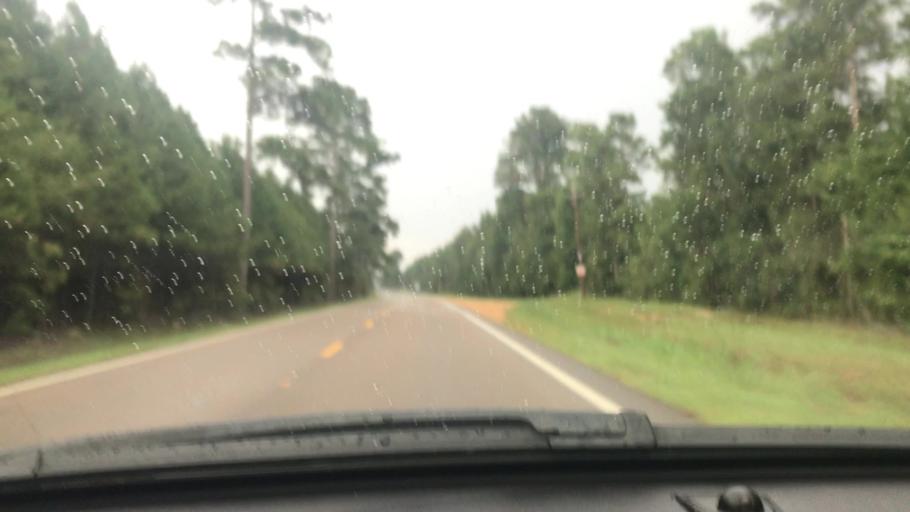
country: US
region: Mississippi
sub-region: Pike County
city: Summit
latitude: 31.3462
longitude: -90.5921
